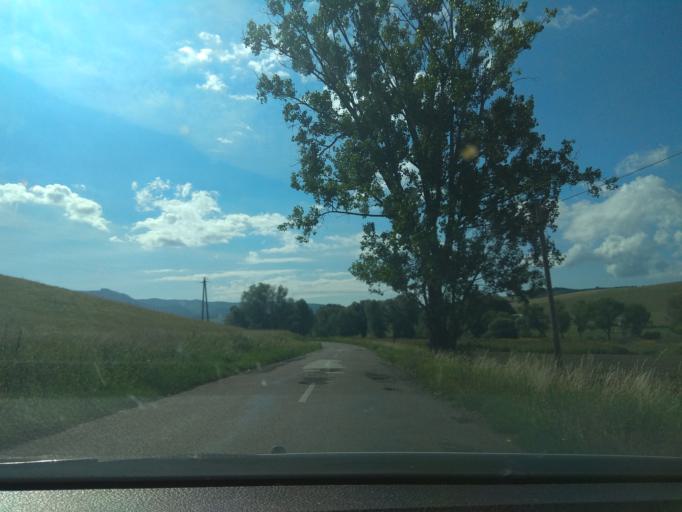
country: HU
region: Borsod-Abauj-Zemplen
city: Borsodnadasd
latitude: 48.0740
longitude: 20.2998
